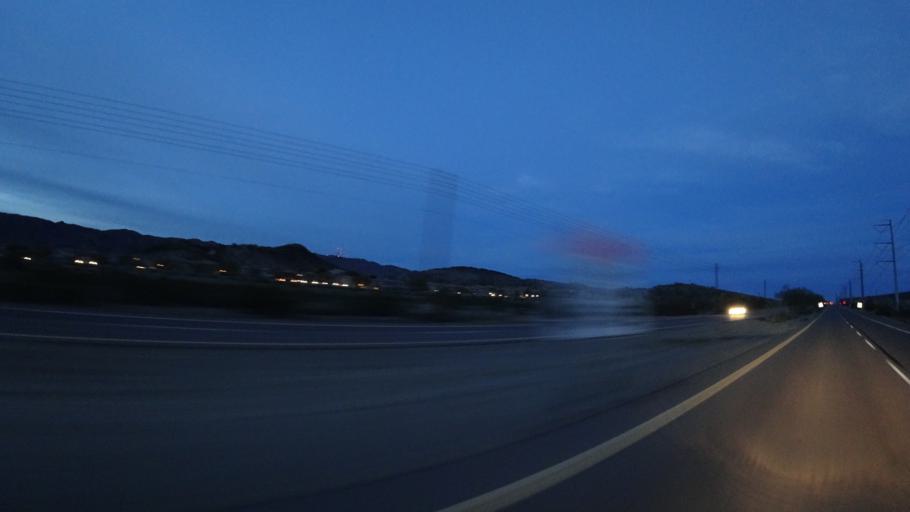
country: US
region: Arizona
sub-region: Maricopa County
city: Laveen
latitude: 33.2909
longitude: -112.0803
